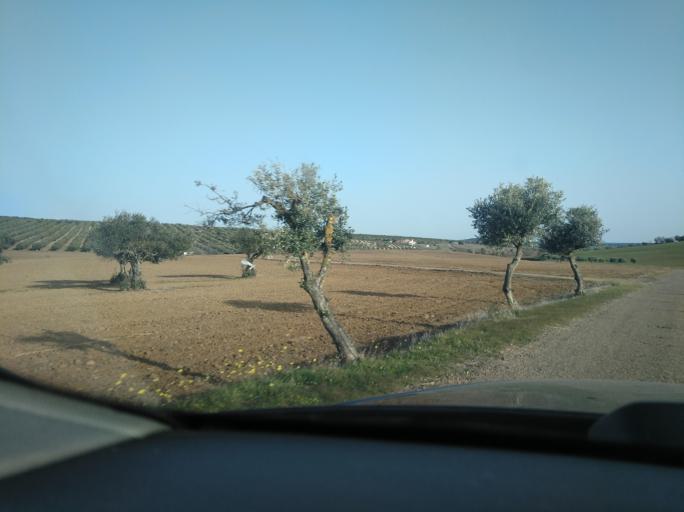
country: PT
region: Portalegre
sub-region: Campo Maior
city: Campo Maior
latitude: 39.0071
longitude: -7.0219
